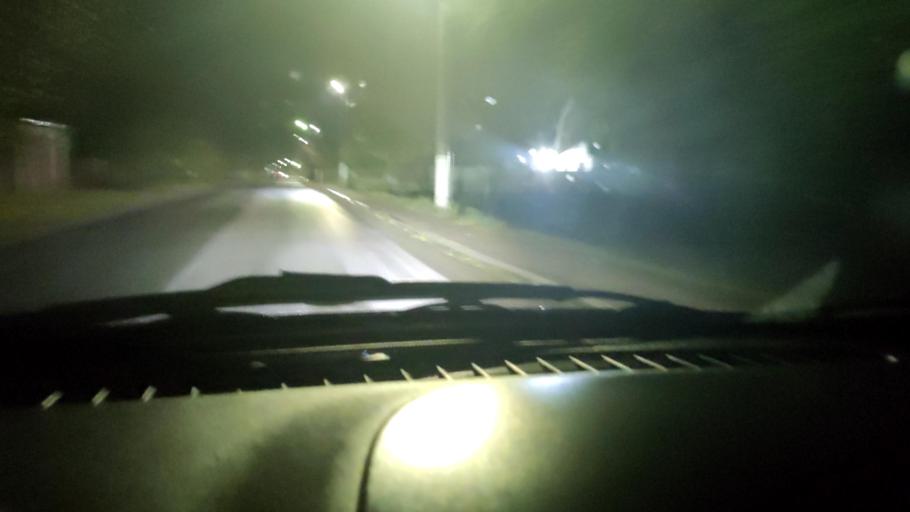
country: RU
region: Voronezj
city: Latnaya
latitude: 51.6588
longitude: 38.9070
